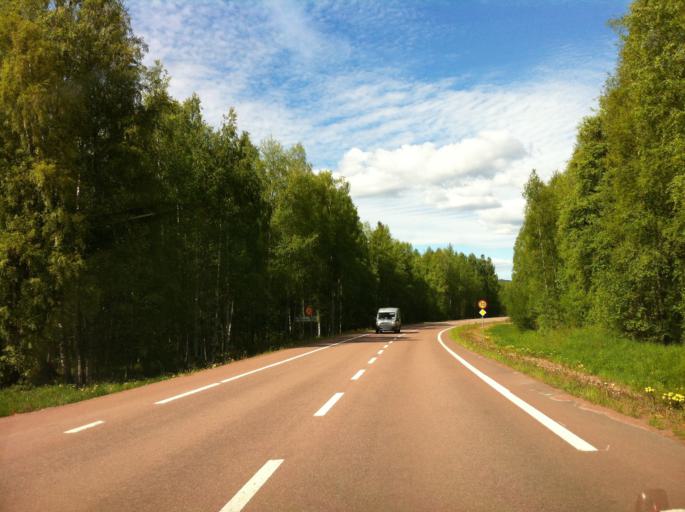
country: SE
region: Dalarna
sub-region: Mora Kommun
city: Mora
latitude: 60.9167
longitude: 14.6077
